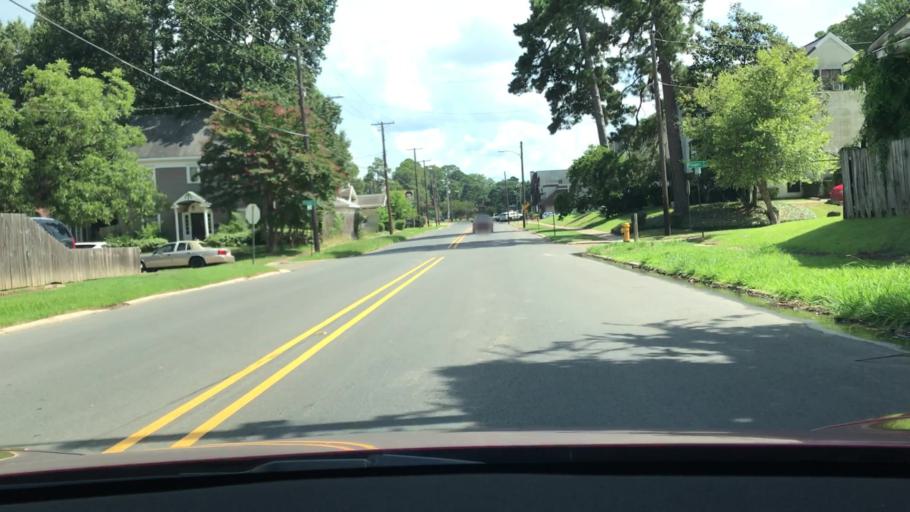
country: US
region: Louisiana
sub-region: Bossier Parish
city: Bossier City
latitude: 32.4879
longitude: -93.7332
